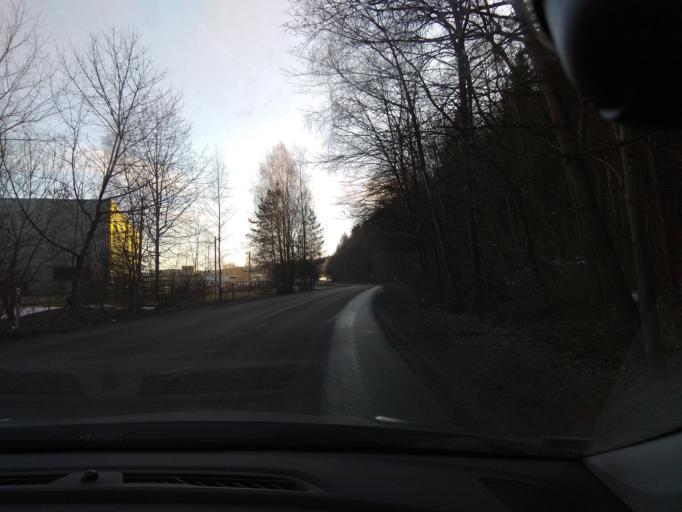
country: LT
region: Vilnius County
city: Lazdynai
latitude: 54.6541
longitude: 25.1818
